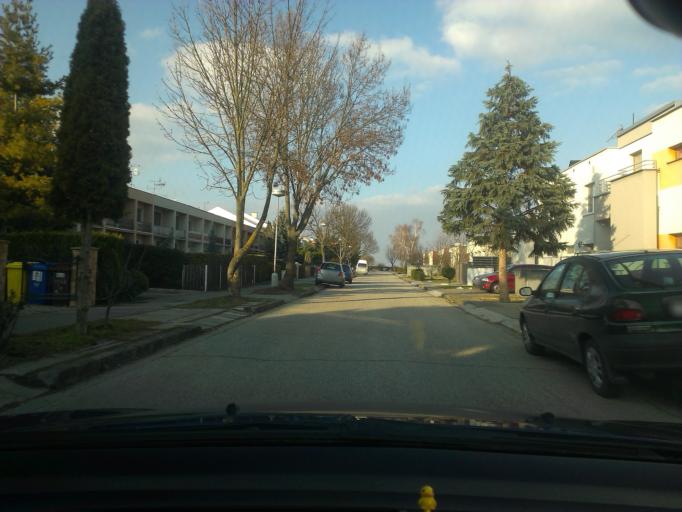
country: SK
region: Trnavsky
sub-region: Okres Trnava
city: Piestany
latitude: 48.6052
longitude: 17.8225
